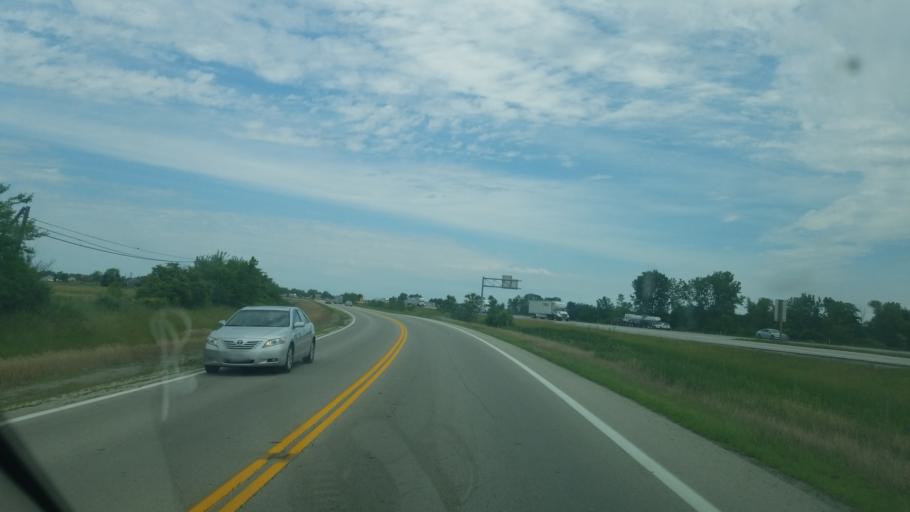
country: US
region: Ohio
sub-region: Wood County
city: North Baltimore
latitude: 41.2431
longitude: -83.6527
